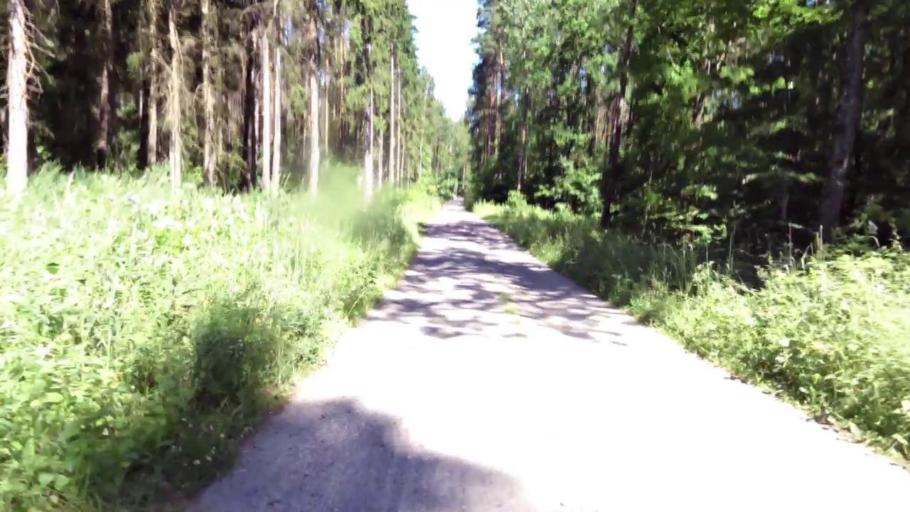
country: PL
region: West Pomeranian Voivodeship
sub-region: Powiat swidwinski
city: Rabino
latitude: 53.8853
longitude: 16.0481
